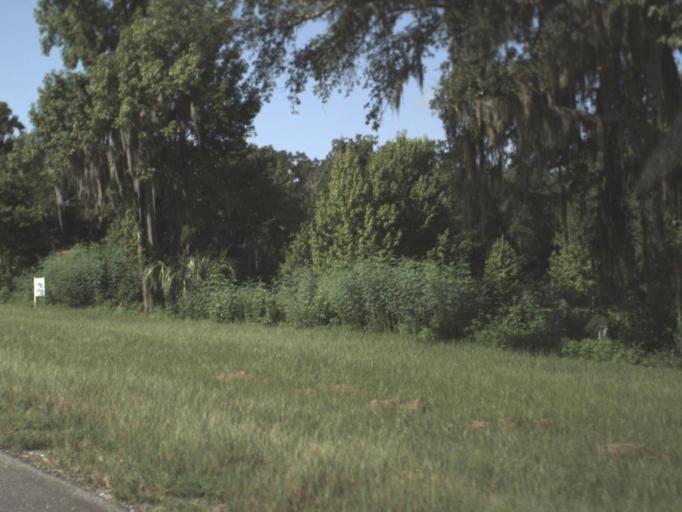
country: US
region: Florida
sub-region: Hernando County
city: North Brooksville
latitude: 28.5862
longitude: -82.4005
